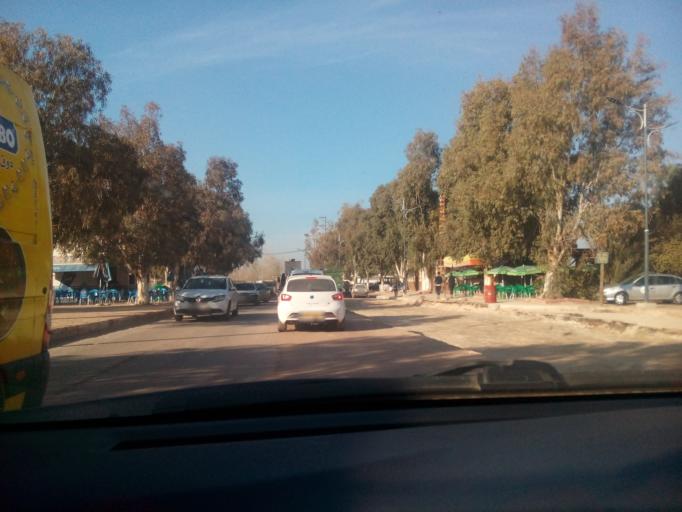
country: DZ
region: Oran
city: Es Senia
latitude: 35.6511
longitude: -0.6128
